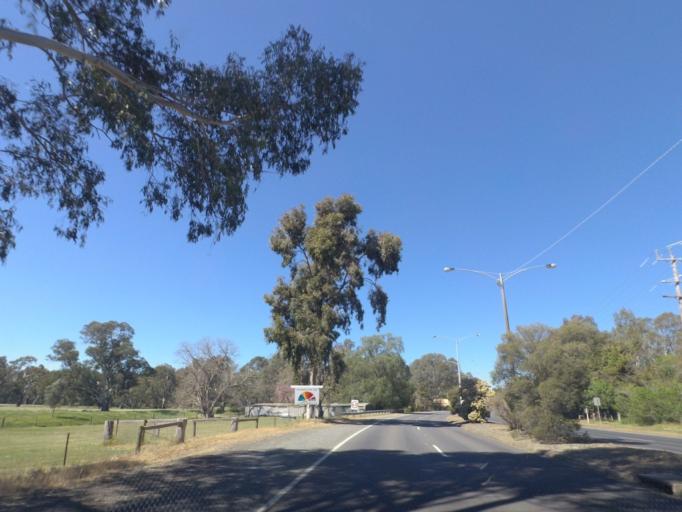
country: AU
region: Victoria
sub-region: Murrindindi
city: Kinglake West
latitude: -37.0214
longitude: 145.1191
